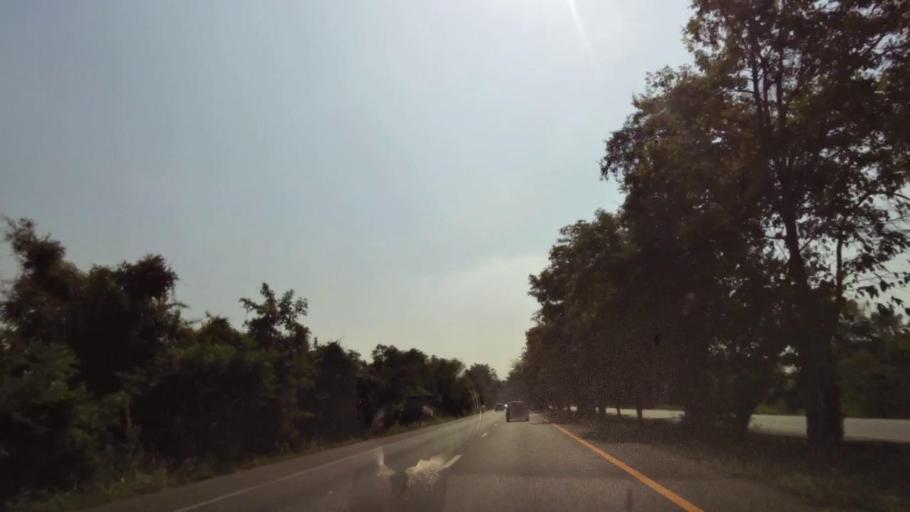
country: TH
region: Phichit
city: Bueng Na Rang
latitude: 16.0288
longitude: 100.1151
